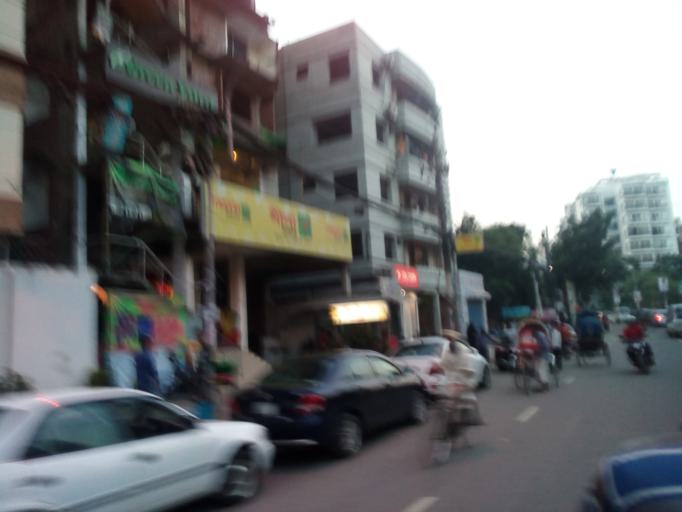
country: BD
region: Dhaka
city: Tungi
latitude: 23.8788
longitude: 90.3908
